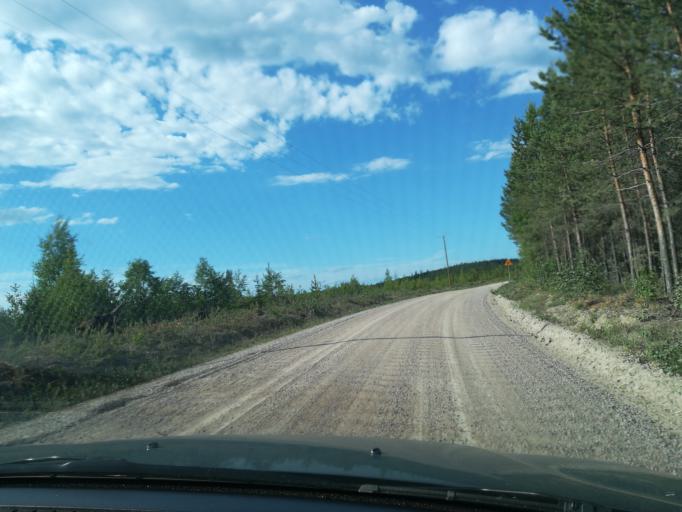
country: FI
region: Southern Savonia
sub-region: Savonlinna
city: Savonlinna
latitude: 61.6309
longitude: 28.7193
